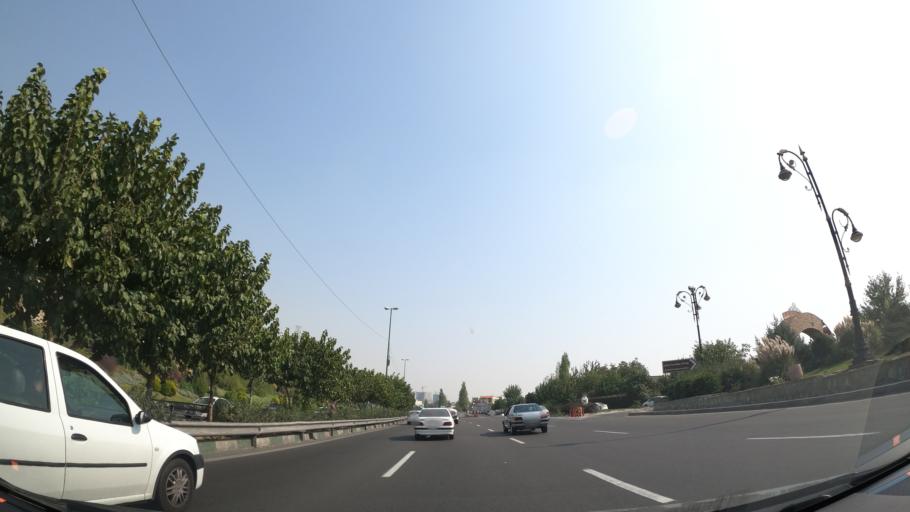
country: IR
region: Tehran
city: Tehran
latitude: 35.7541
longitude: 51.2731
